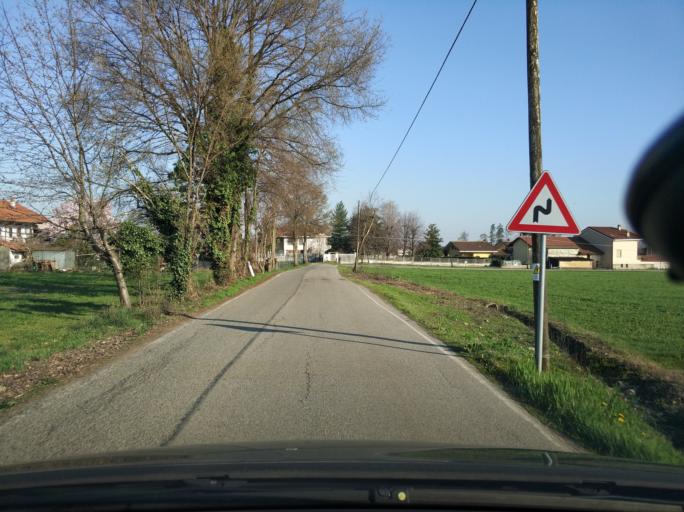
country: IT
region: Piedmont
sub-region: Provincia di Torino
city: Cirie
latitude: 45.2013
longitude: 7.6040
